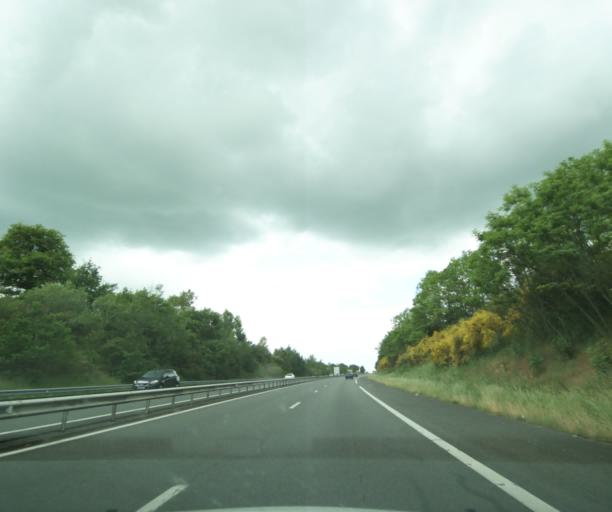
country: FR
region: Auvergne
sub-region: Departement de l'Allier
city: Montmarault
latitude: 46.3338
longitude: 2.8905
